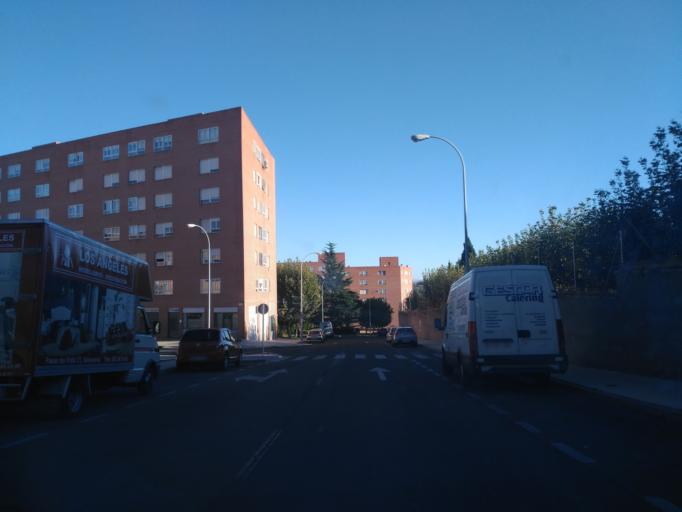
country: ES
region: Castille and Leon
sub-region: Provincia de Salamanca
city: Salamanca
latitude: 40.9680
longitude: -5.6463
